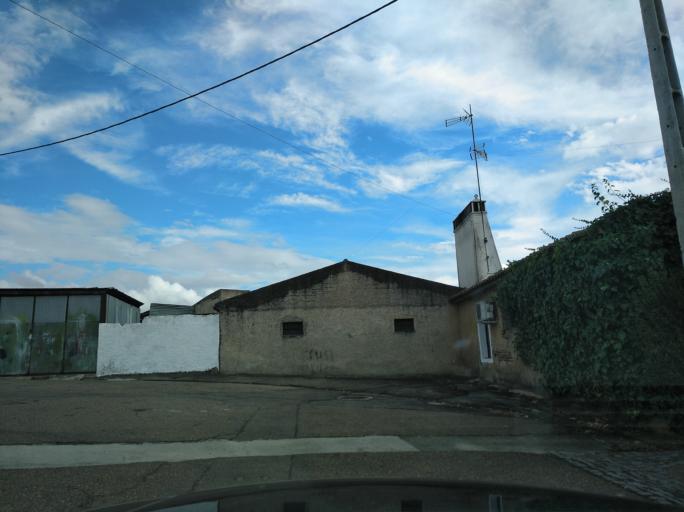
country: PT
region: Portalegre
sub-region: Campo Maior
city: Campo Maior
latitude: 39.0589
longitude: -7.1252
